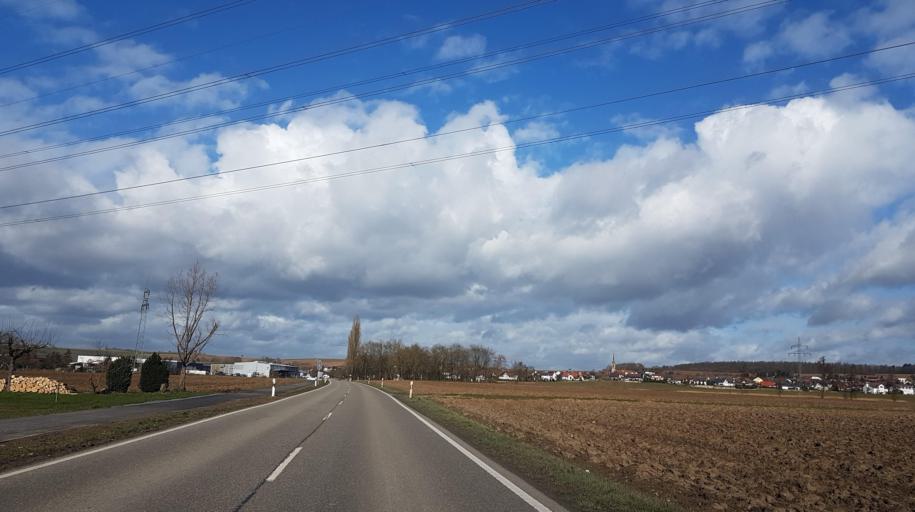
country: DE
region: Baden-Wuerttemberg
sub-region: Regierungsbezirk Stuttgart
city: Neuenstadt am Kocher
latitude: 49.2500
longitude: 9.3044
